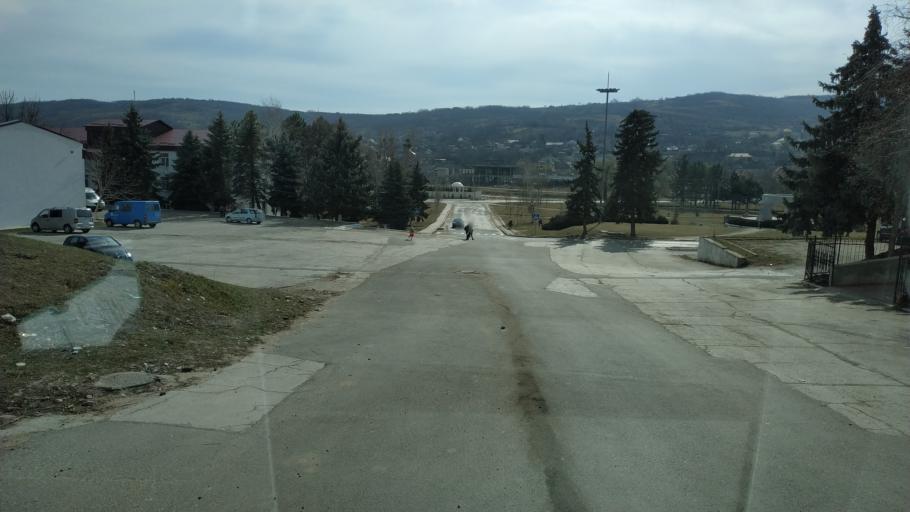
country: MD
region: Chisinau
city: Vatra
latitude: 47.0948
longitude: 28.6656
